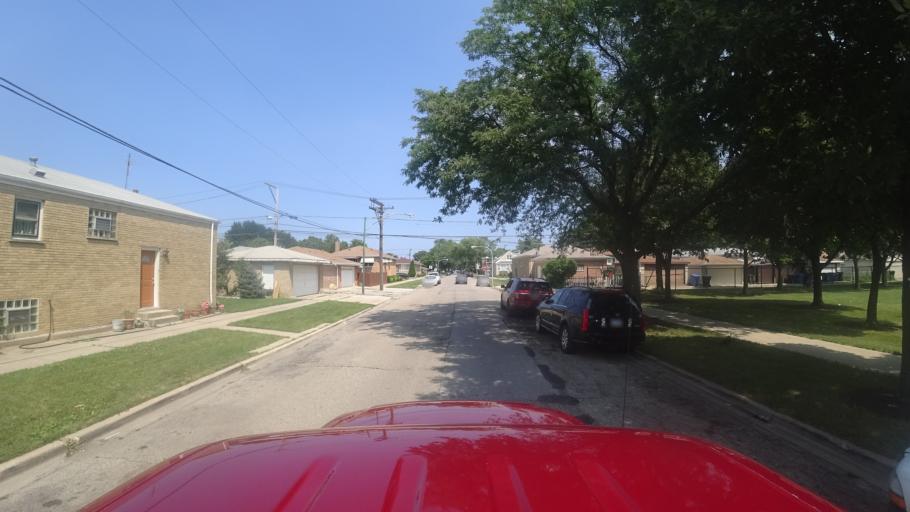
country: US
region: Illinois
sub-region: Cook County
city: Cicero
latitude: 41.8059
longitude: -87.7343
